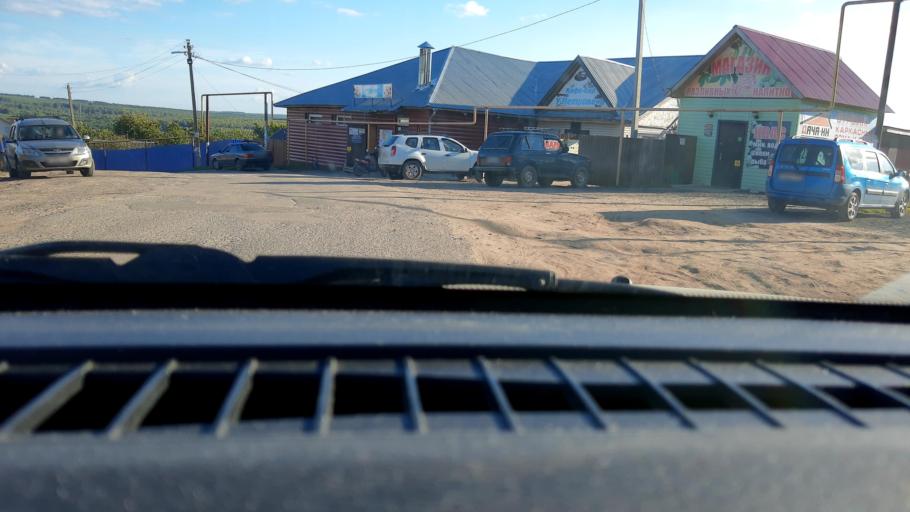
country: RU
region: Nizjnij Novgorod
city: Surovatikha
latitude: 55.9335
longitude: 43.8788
